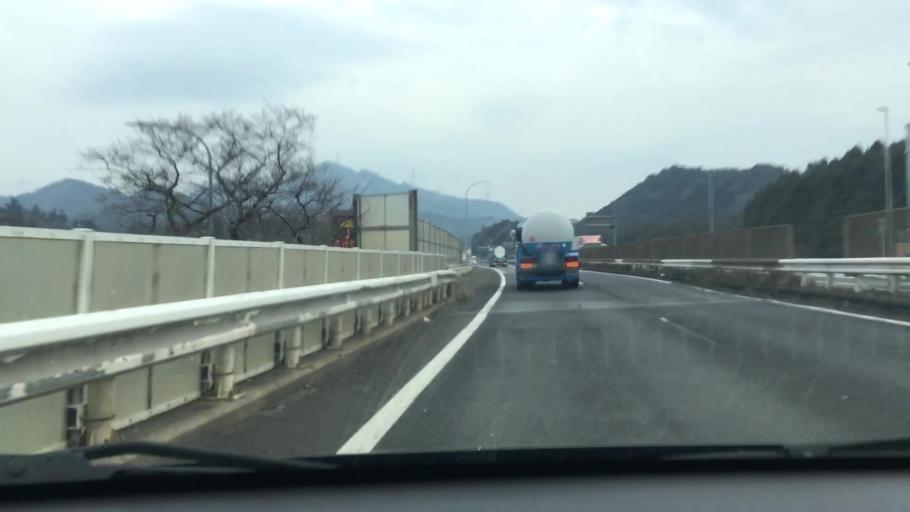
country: JP
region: Mie
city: Kameyama
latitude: 34.8366
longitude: 136.3109
